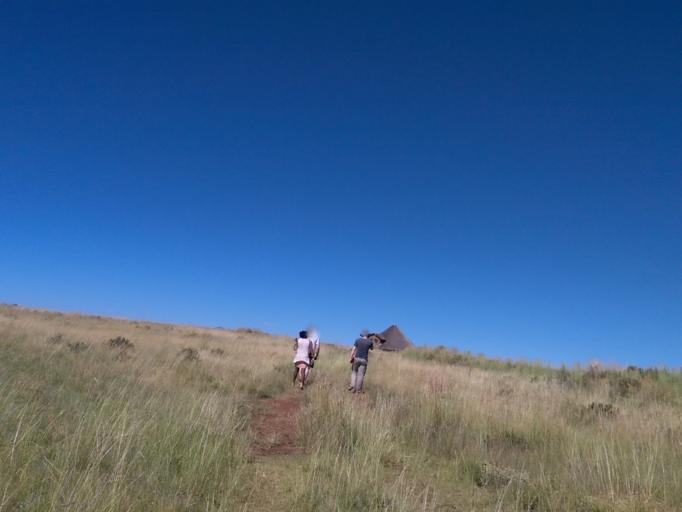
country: LS
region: Maseru
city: Maseru
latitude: -29.4829
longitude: 27.5822
